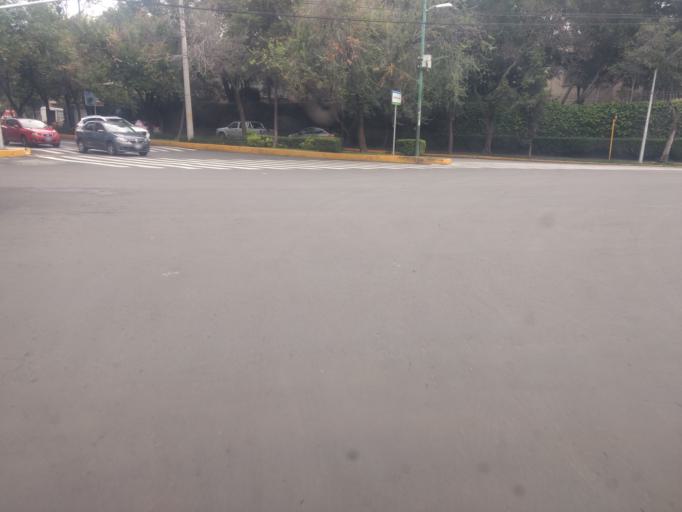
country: MX
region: Mexico City
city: Alvaro Obregon
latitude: 19.3664
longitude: -99.1833
